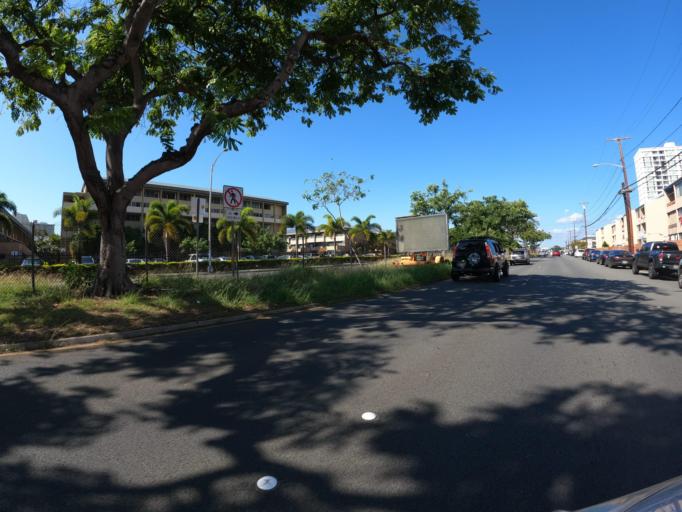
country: US
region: Hawaii
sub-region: Honolulu County
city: Honolulu
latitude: 21.3184
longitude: -157.8605
